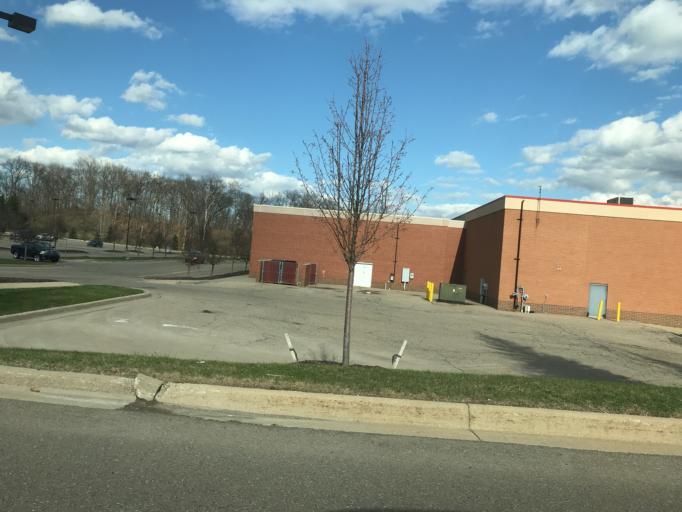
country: US
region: Michigan
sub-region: Livingston County
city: Brighton
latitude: 42.5476
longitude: -83.7960
